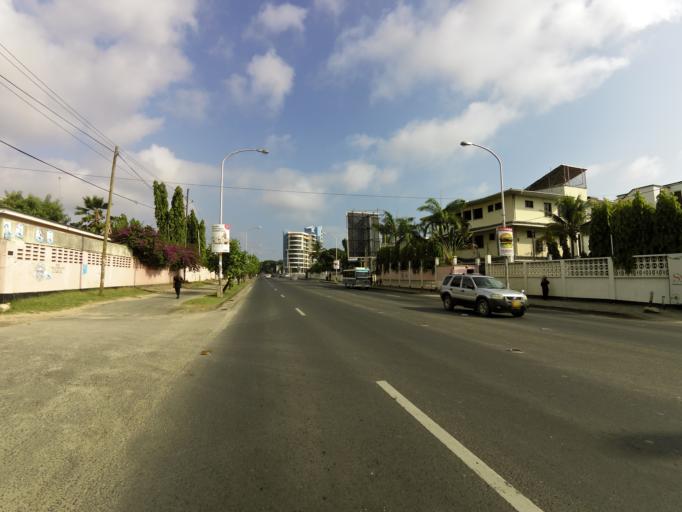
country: TZ
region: Dar es Salaam
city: Dar es Salaam
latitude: -6.8072
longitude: 39.2864
